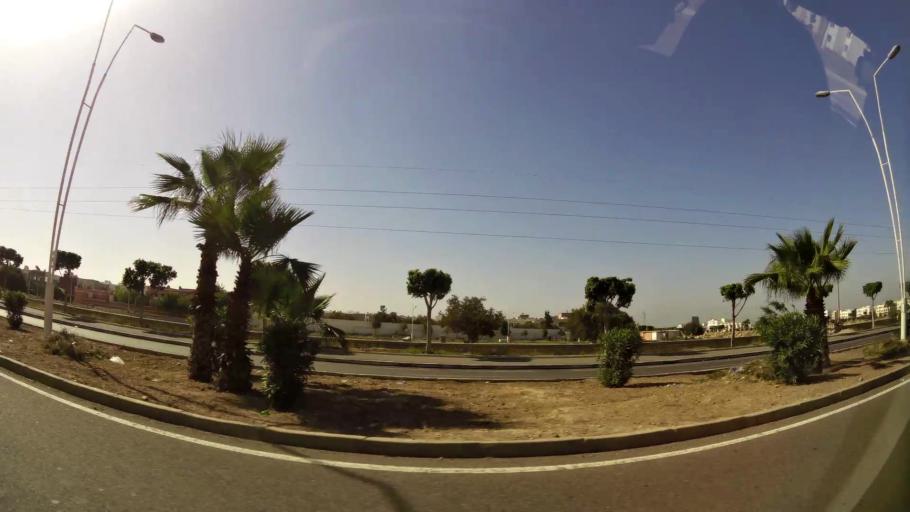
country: MA
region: Souss-Massa-Draa
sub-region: Inezgane-Ait Mellou
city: Inezgane
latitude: 30.3849
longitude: -9.5036
